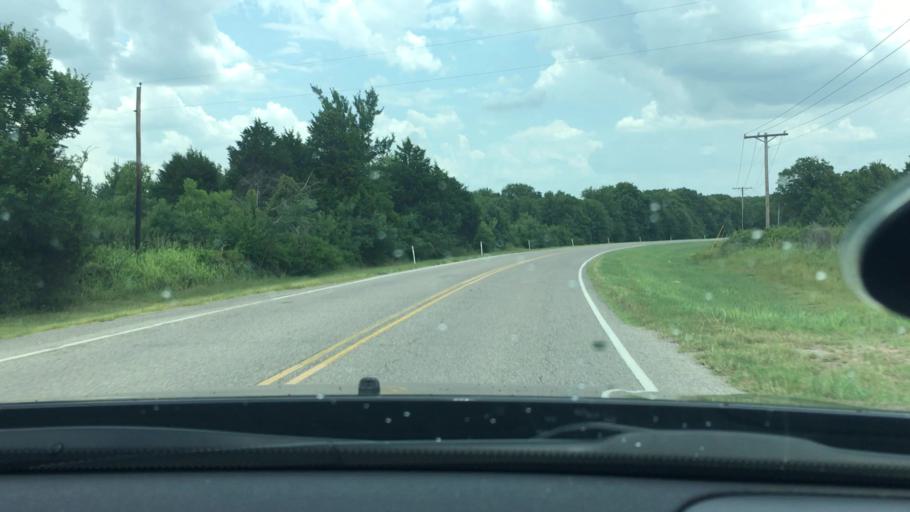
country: US
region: Oklahoma
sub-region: Love County
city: Marietta
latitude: 33.9681
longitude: -97.0220
